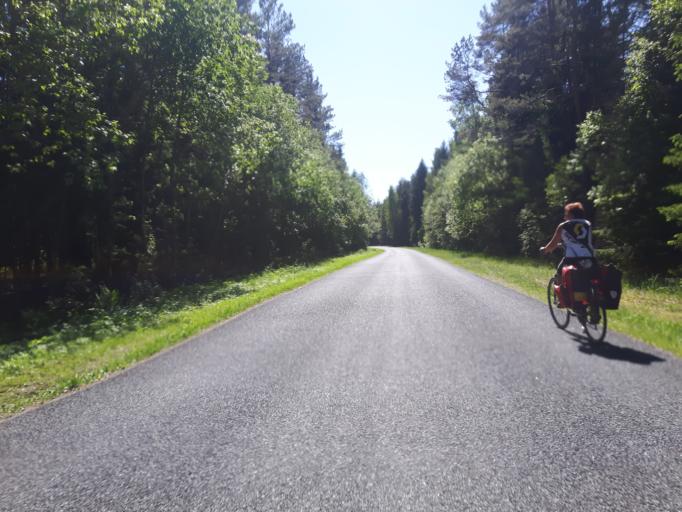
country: EE
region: Laeaene-Virumaa
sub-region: Haljala vald
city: Haljala
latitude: 59.5666
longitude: 26.2430
